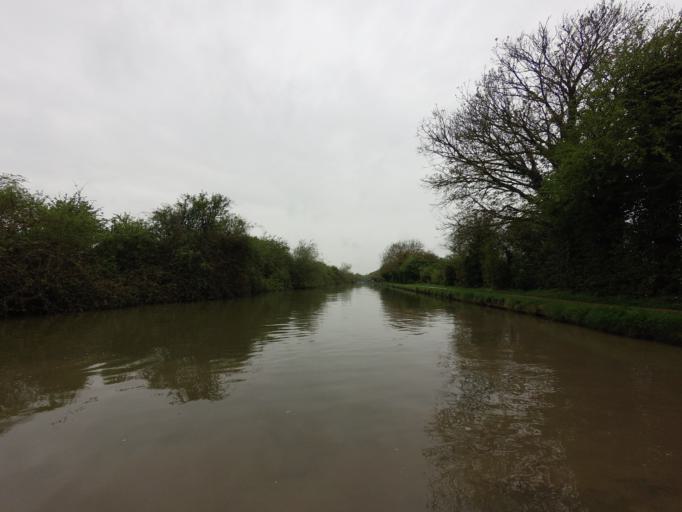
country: GB
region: England
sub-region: Milton Keynes
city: Stony Stratford
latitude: 52.0678
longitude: -0.8317
